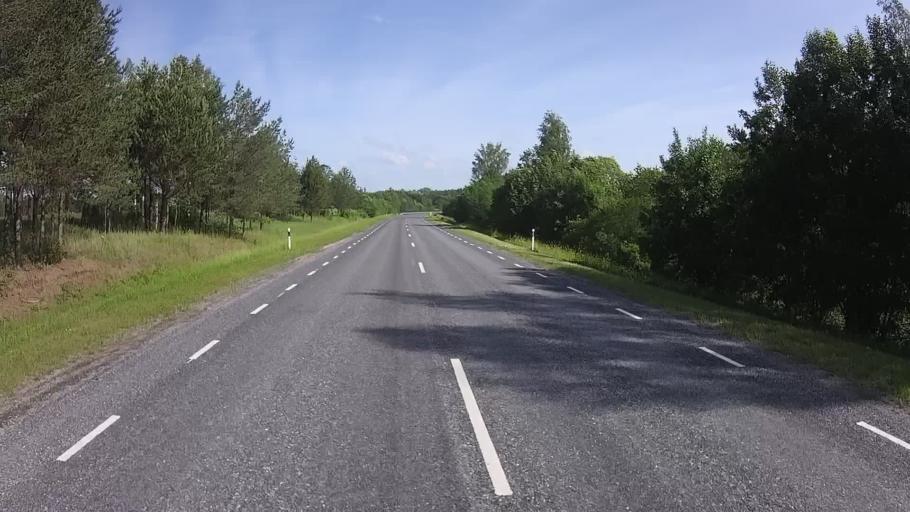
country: EE
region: Valgamaa
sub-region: Torva linn
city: Torva
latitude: 58.0363
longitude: 25.9709
